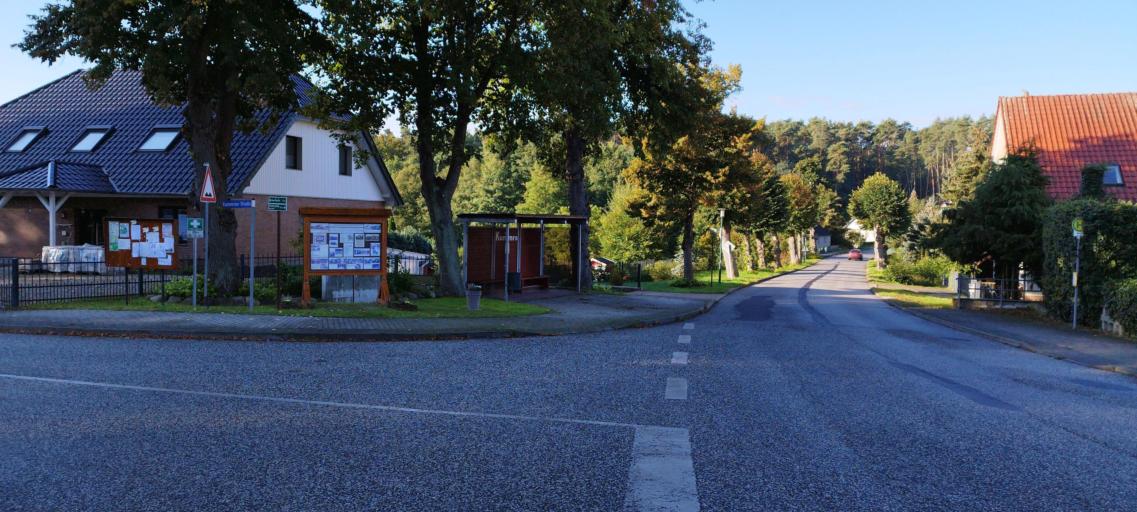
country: DE
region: Brandenburg
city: Neuzelle
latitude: 52.0816
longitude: 14.6233
